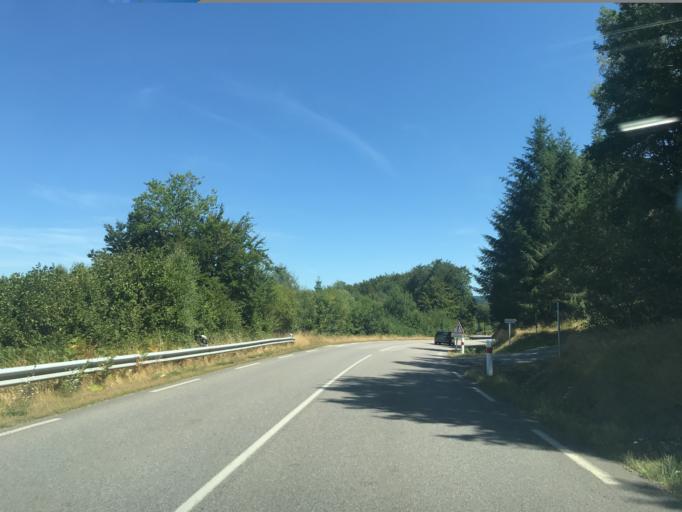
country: FR
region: Limousin
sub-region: Departement de la Correze
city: Meymac
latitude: 45.4583
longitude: 2.1244
